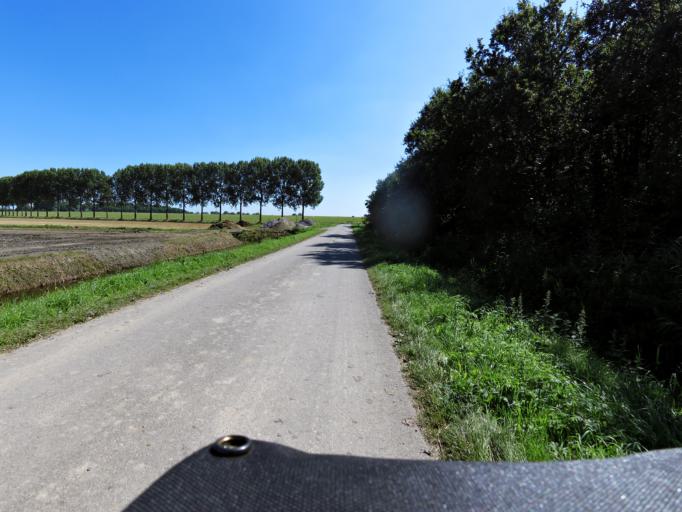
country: NL
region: South Holland
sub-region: Gemeente Dordrecht
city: Dordrecht
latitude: 51.7522
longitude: 4.7025
